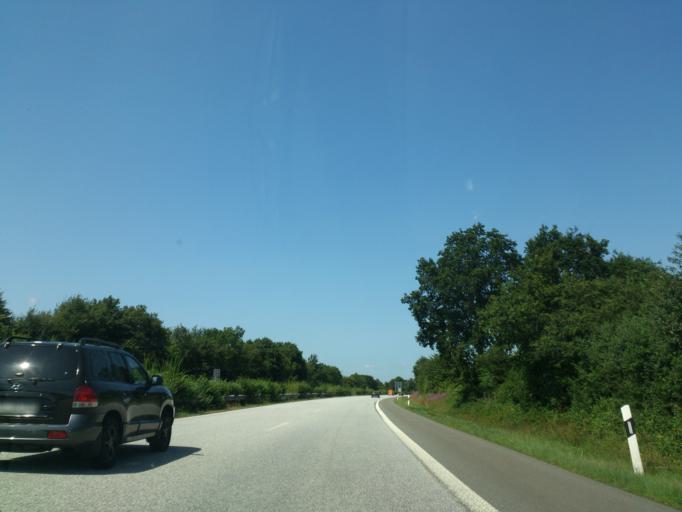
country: DE
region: Schleswig-Holstein
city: Schafstedt
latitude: 54.0760
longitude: 9.2803
